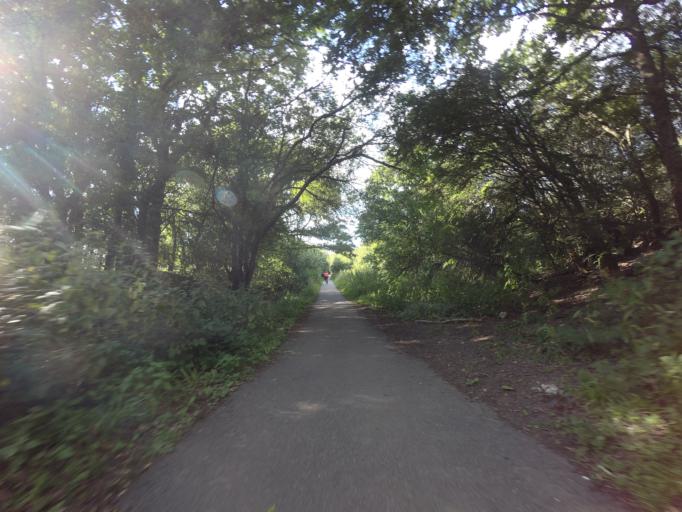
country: GB
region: England
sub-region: East Sussex
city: Horam
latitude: 50.9164
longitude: 0.2576
